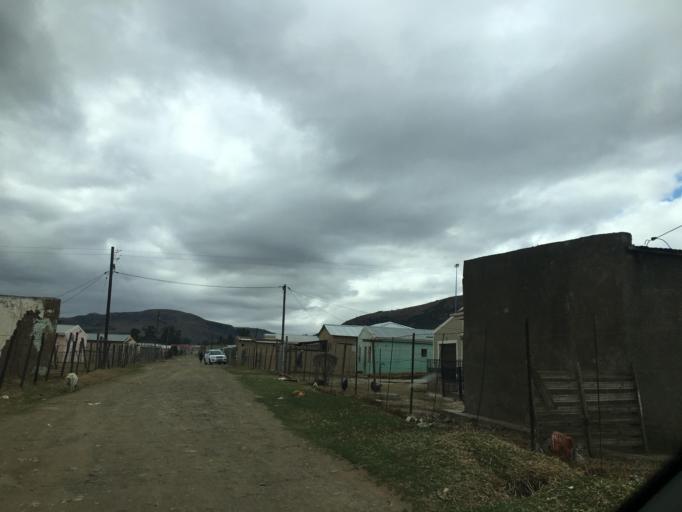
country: ZA
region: Eastern Cape
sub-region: Chris Hani District Municipality
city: Cala
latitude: -31.5350
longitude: 27.7002
